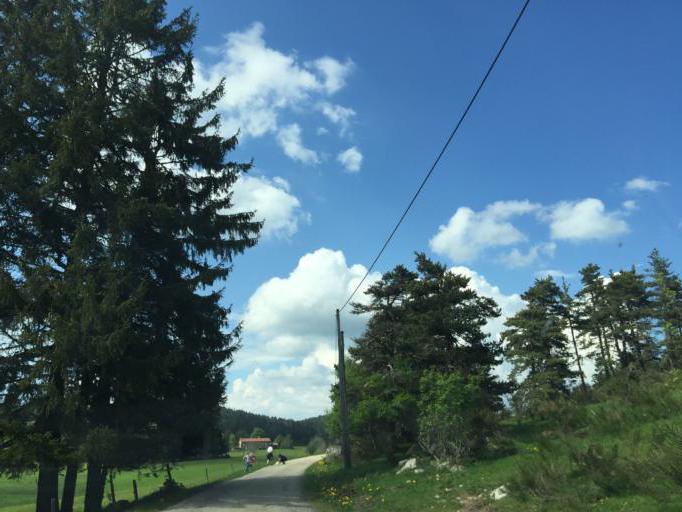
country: FR
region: Rhone-Alpes
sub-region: Departement de la Loire
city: Saint-Sauveur-en-Rue
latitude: 45.3014
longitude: 4.4786
